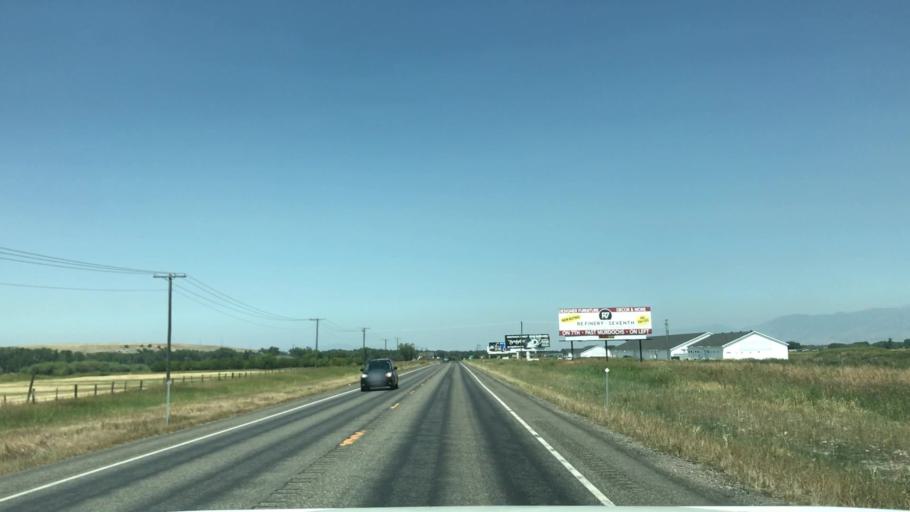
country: US
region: Montana
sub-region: Gallatin County
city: Four Corners
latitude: 45.6325
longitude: -111.1968
